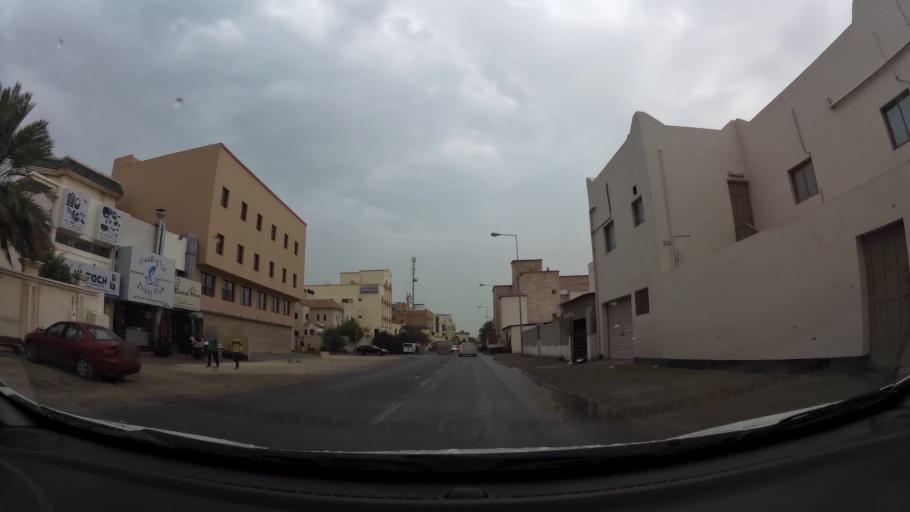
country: BH
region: Northern
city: Madinat `Isa
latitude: 26.1627
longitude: 50.5722
